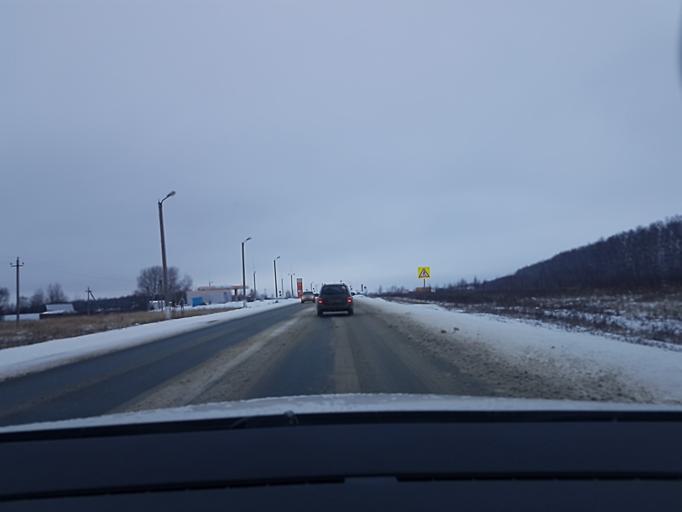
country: RU
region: Moskovskaya
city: Uzunovo
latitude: 54.5806
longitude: 38.4420
